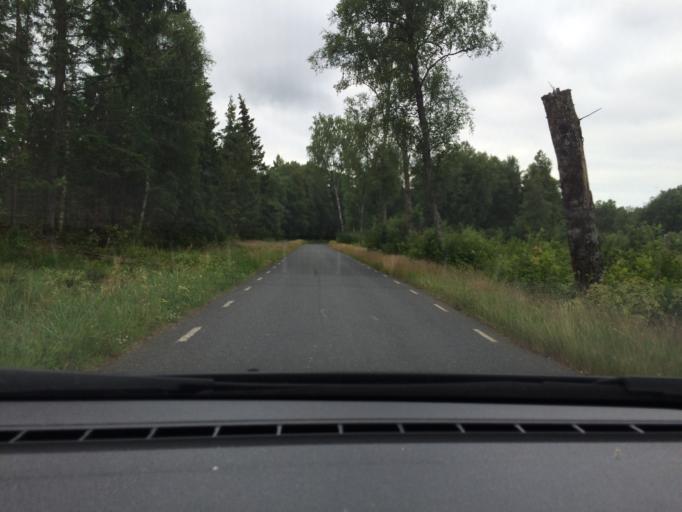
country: SE
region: Joenkoeping
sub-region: Varnamo Kommun
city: Forsheda
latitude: 57.0809
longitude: 13.8137
